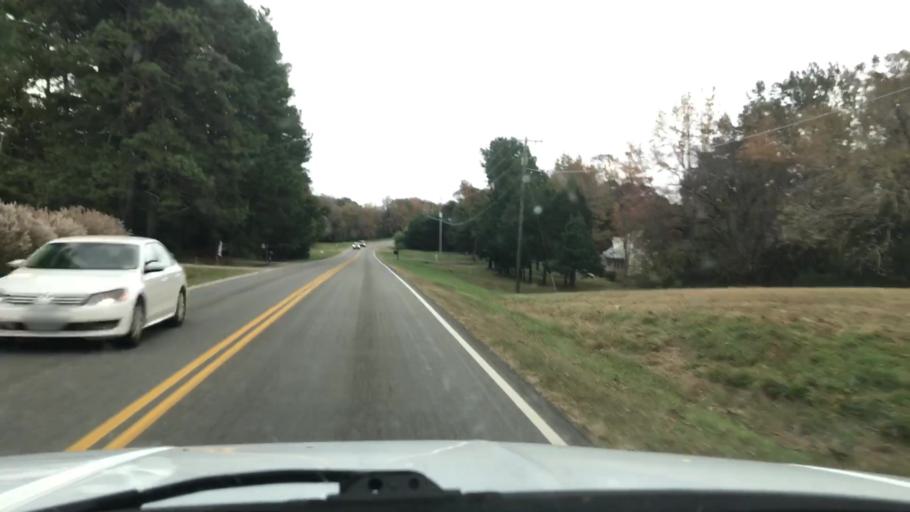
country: US
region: Virginia
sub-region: Goochland County
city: Goochland
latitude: 37.6659
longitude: -77.8765
